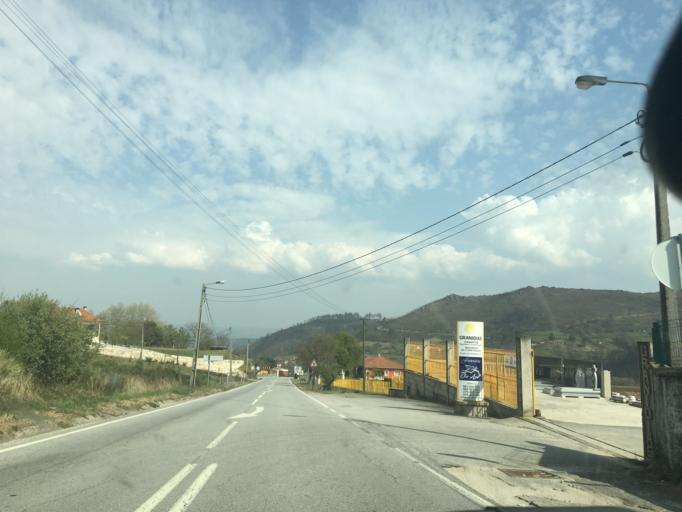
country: PT
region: Vila Real
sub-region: Boticas
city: Boticas
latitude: 41.6821
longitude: -7.6976
